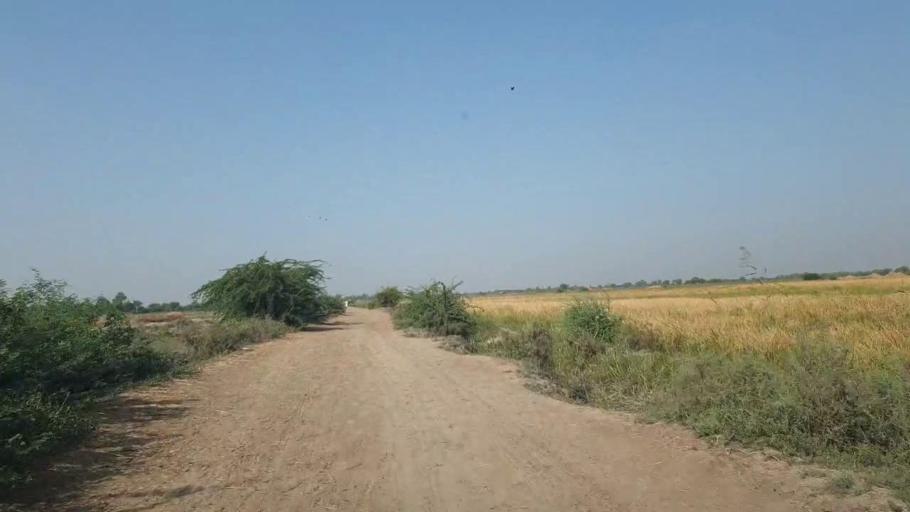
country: PK
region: Sindh
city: Badin
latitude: 24.5230
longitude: 68.7580
